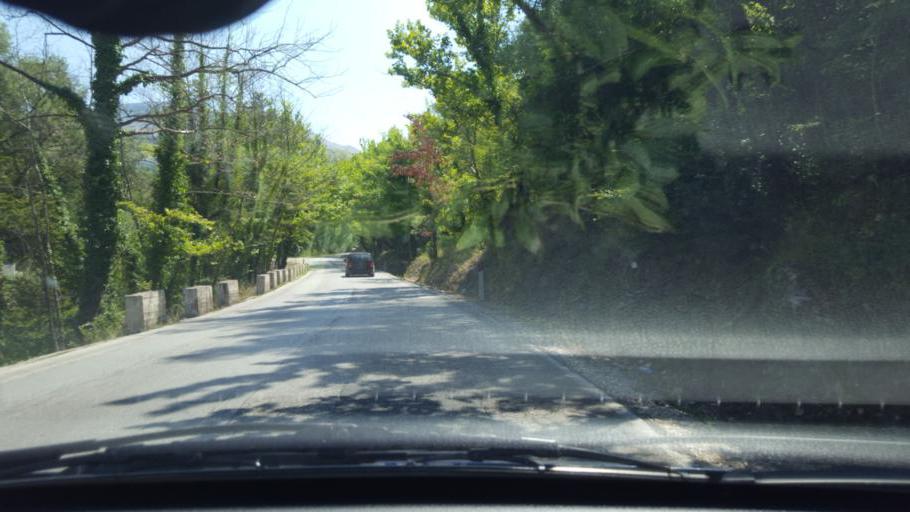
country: AL
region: Vlore
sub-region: Rrethi i Delvines
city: Mesopotam
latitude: 39.9202
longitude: 20.1677
